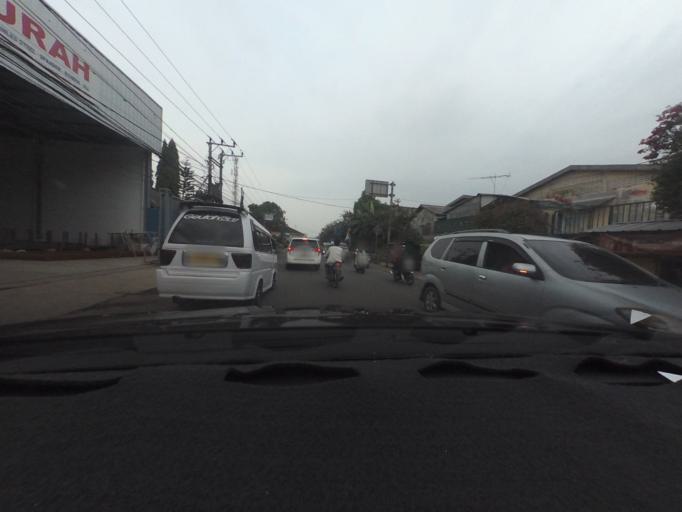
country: ID
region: West Java
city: Cicurug
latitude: -6.7961
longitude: 106.7777
